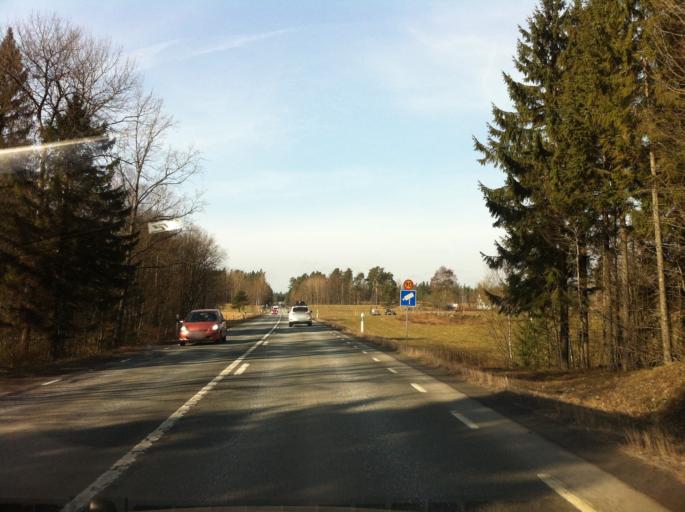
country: SE
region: Joenkoeping
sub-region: Jonkopings Kommun
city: Bankeryd
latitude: 57.8403
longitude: 14.0614
